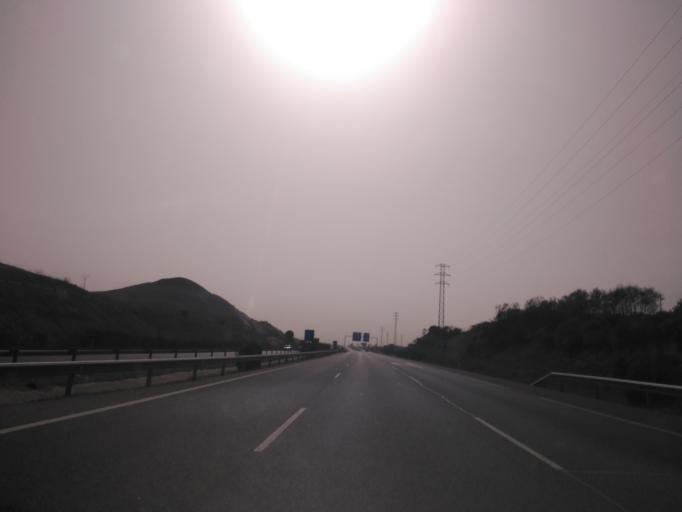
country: ES
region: Castille and Leon
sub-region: Provincia de Palencia
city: Palencia
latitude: 41.9911
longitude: -4.5029
